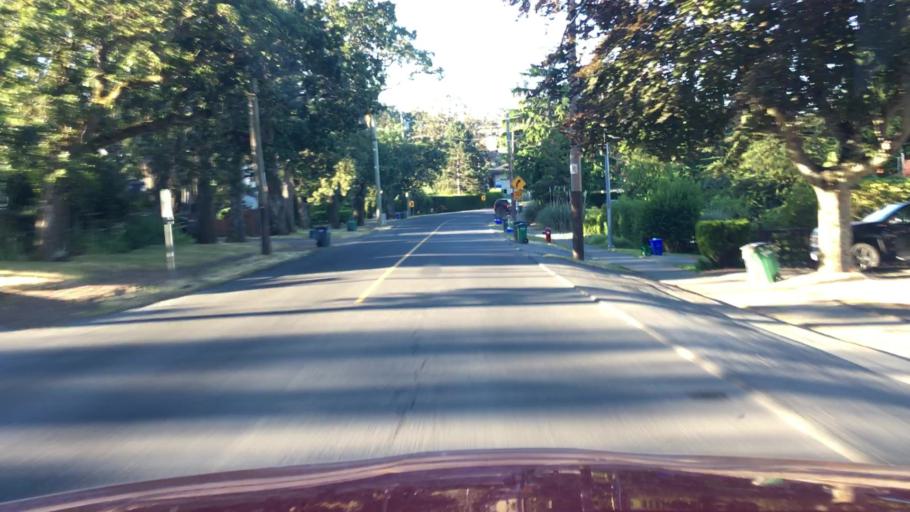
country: CA
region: British Columbia
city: Oak Bay
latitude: 48.4499
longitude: -123.3255
